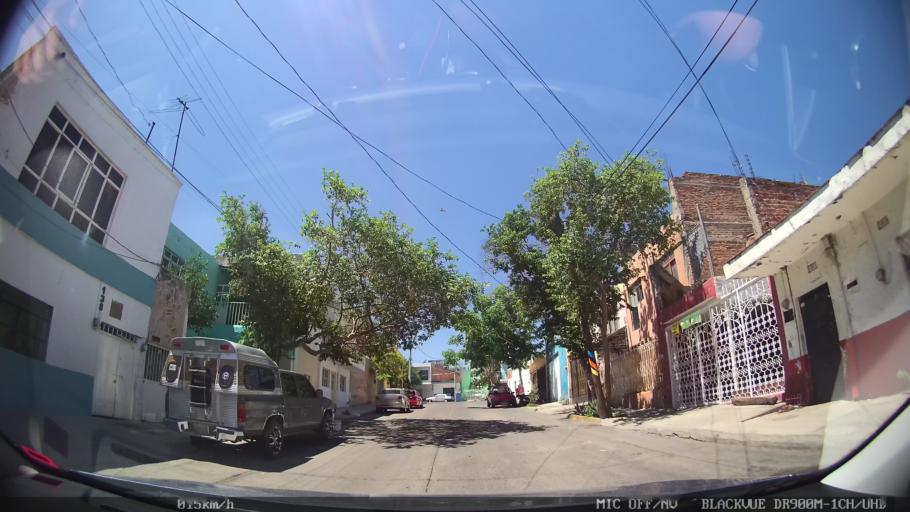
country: MX
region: Jalisco
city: Tlaquepaque
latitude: 20.6911
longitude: -103.2937
